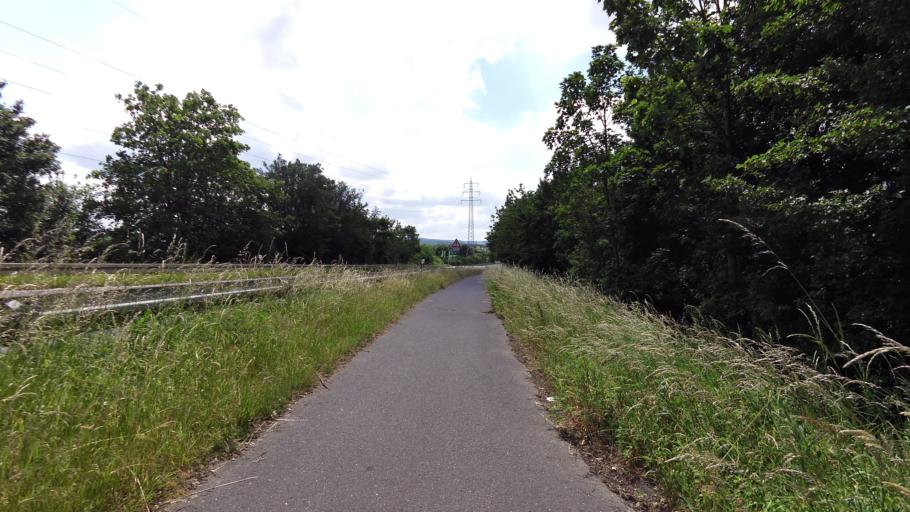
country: DE
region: North Rhine-Westphalia
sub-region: Regierungsbezirk Koln
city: Rheinbach
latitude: 50.6355
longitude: 6.9599
